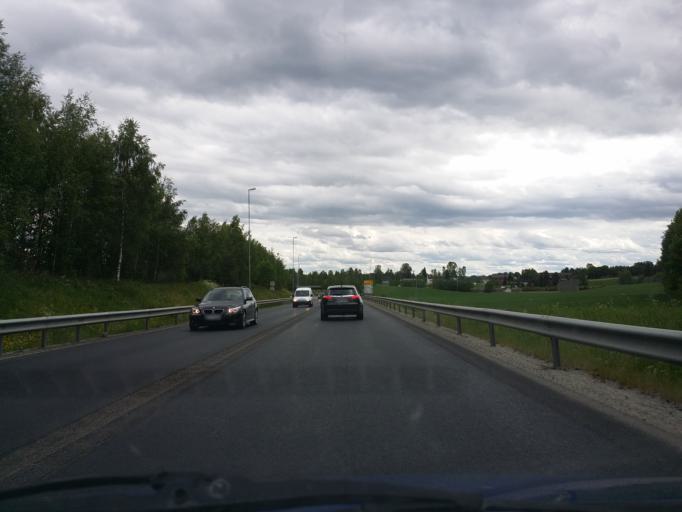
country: NO
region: Hedmark
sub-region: Hamar
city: Hamar
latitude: 60.8370
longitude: 11.0714
